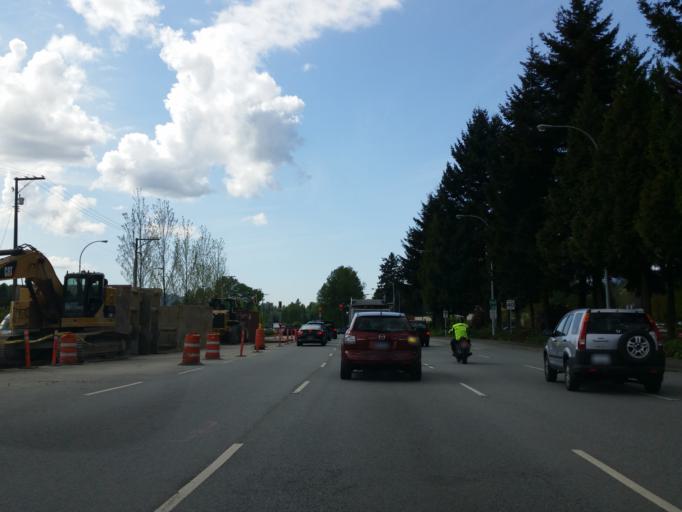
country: CA
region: British Columbia
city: Coquitlam
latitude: 49.2769
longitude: -122.7994
